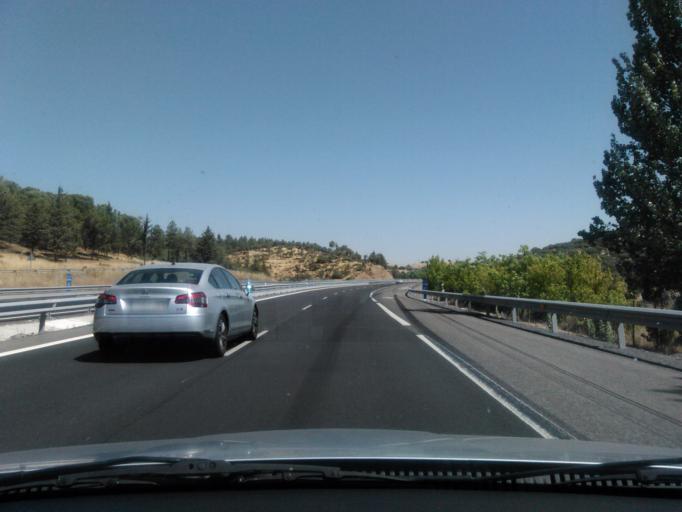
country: ES
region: Castille-La Mancha
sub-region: Provincia de Ciudad Real
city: Viso del Marques
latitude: 38.4440
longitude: -3.4964
